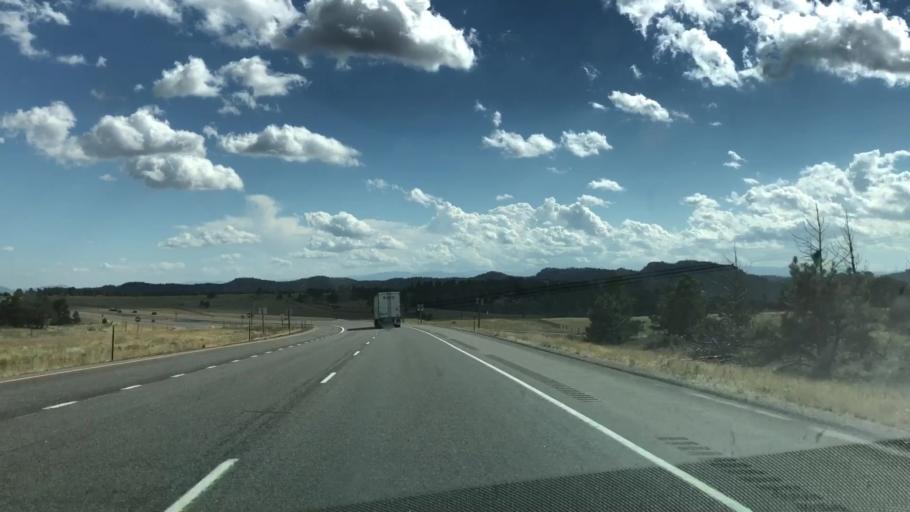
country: US
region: Wyoming
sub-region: Albany County
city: Laramie
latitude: 41.0111
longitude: -105.4200
